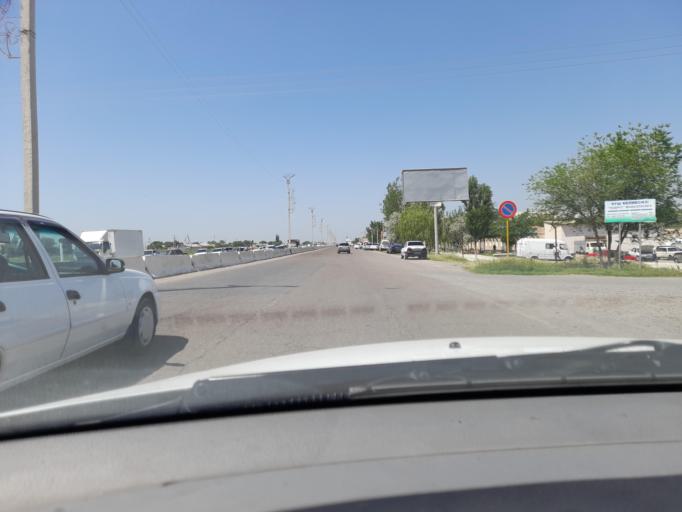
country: UZ
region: Sirdaryo
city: Guliston
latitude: 40.4912
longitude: 68.7070
